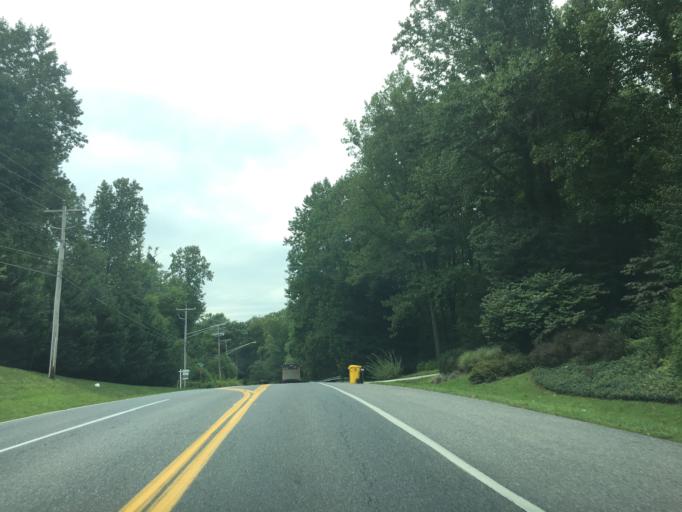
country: US
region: Maryland
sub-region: Anne Arundel County
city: Crownsville
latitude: 39.0424
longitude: -76.5904
